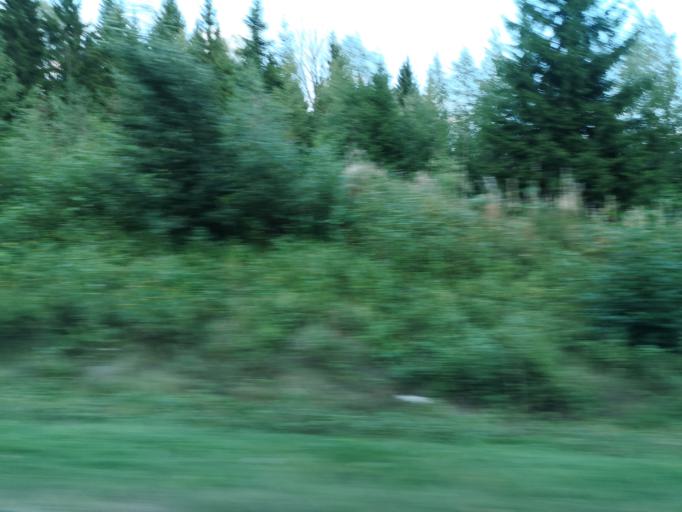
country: FI
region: Paijanne Tavastia
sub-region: Lahti
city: Hartola
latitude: 61.5969
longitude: 26.0080
